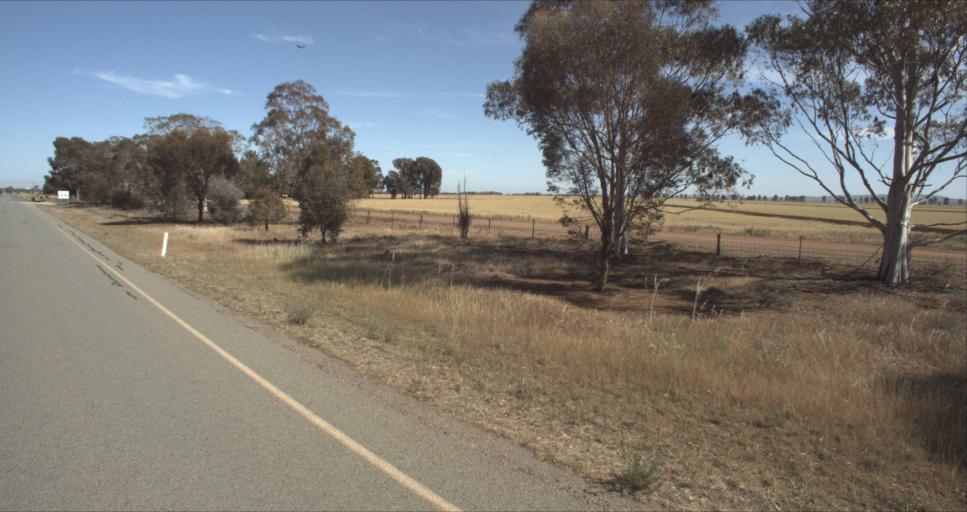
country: AU
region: New South Wales
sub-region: Leeton
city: Leeton
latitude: -34.5592
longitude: 146.4709
